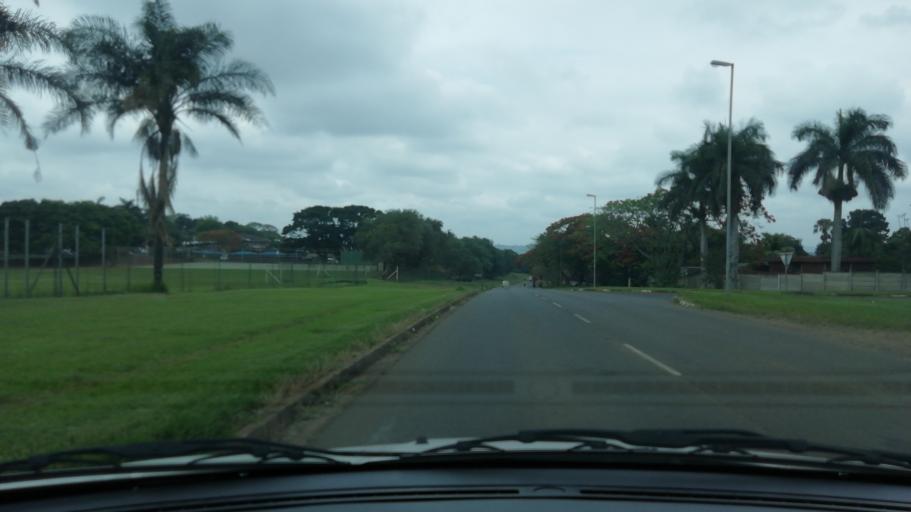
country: ZA
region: KwaZulu-Natal
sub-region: uThungulu District Municipality
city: Empangeni
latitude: -28.7516
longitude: 31.8852
